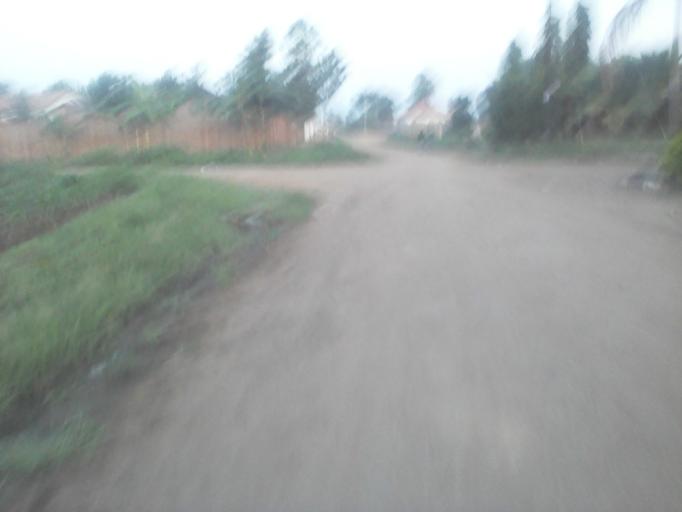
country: UG
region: Eastern Region
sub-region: Mbale District
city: Mbale
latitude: 1.0854
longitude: 34.1752
